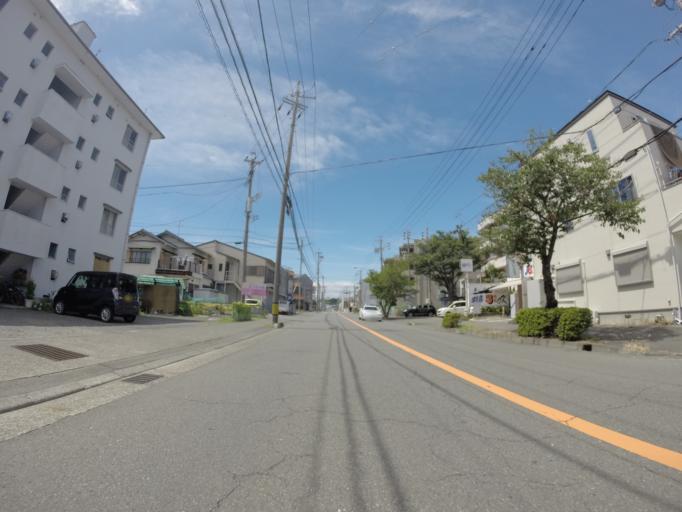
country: JP
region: Shizuoka
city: Shizuoka-shi
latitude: 34.9988
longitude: 138.4750
